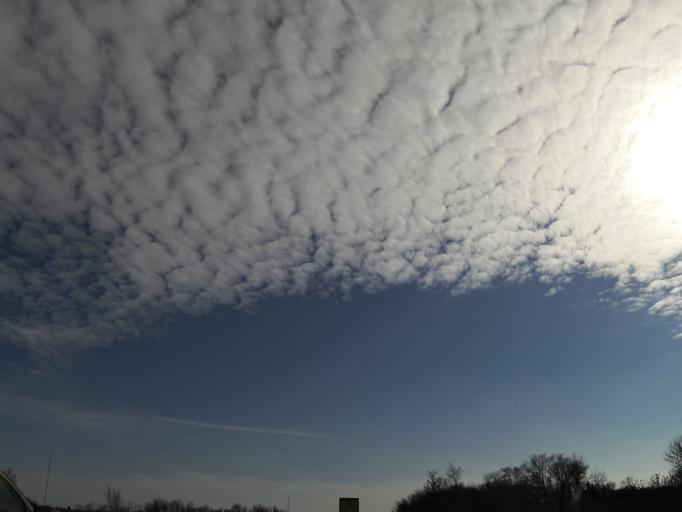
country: US
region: Minnesota
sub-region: Steele County
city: Medford
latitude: 44.1890
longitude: -93.2558
